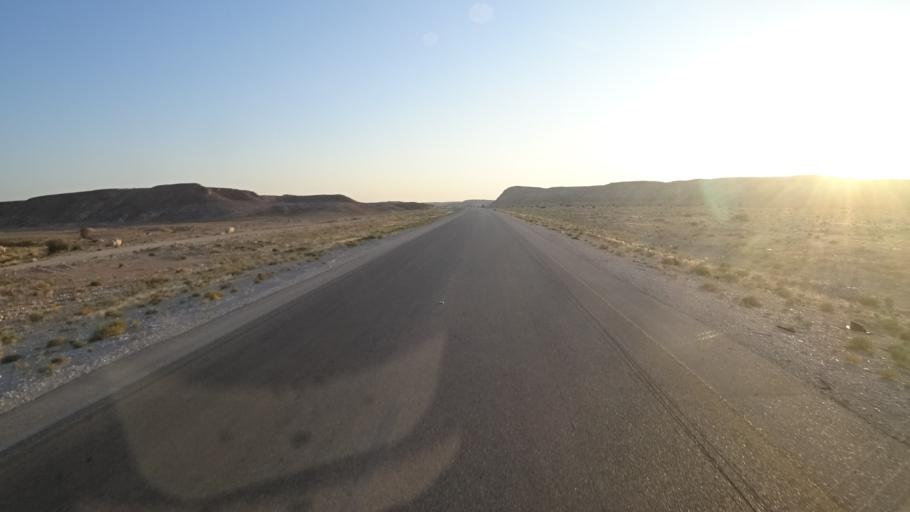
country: OM
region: Zufar
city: Salalah
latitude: 17.5282
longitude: 53.3813
